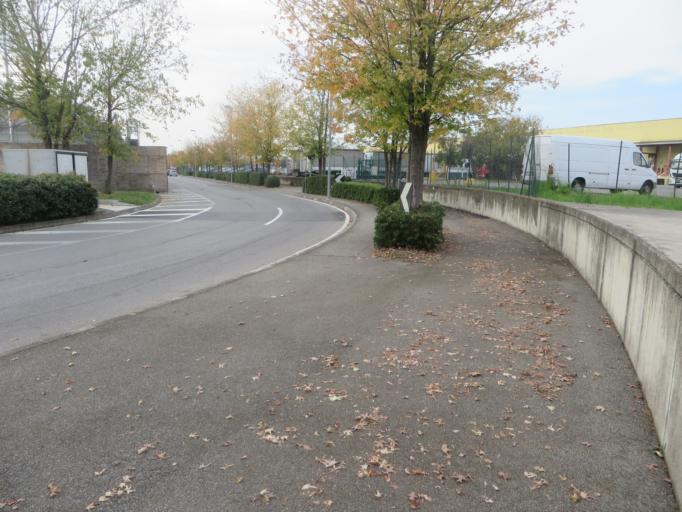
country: IT
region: Lombardy
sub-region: Provincia di Brescia
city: Castegnato
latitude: 45.5786
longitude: 10.1214
